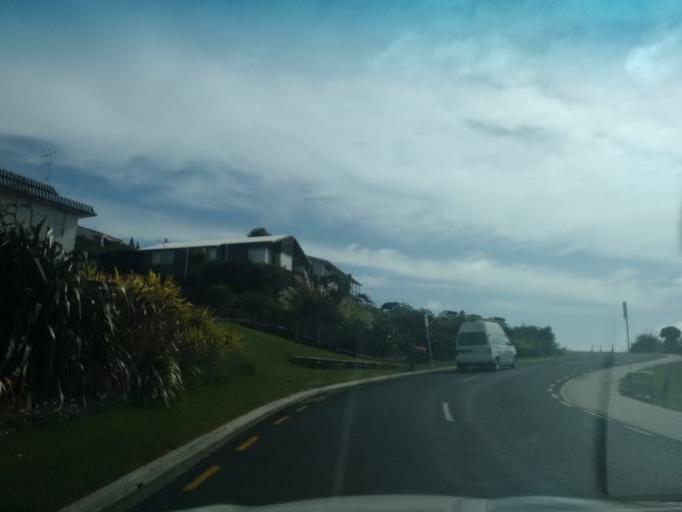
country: NZ
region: Waikato
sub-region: Thames-Coromandel District
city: Whitianga
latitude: -36.8378
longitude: 175.8004
